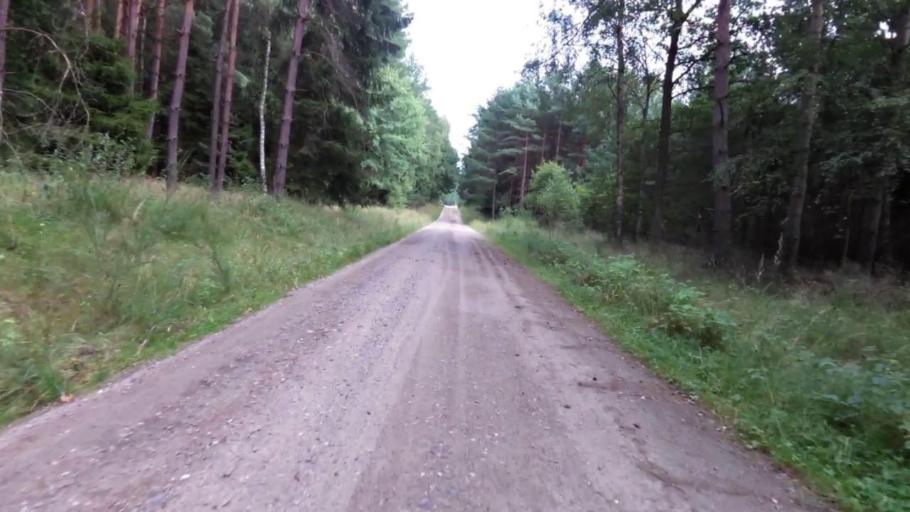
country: PL
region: West Pomeranian Voivodeship
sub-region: Powiat drawski
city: Drawsko Pomorskie
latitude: 53.5624
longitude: 15.8852
